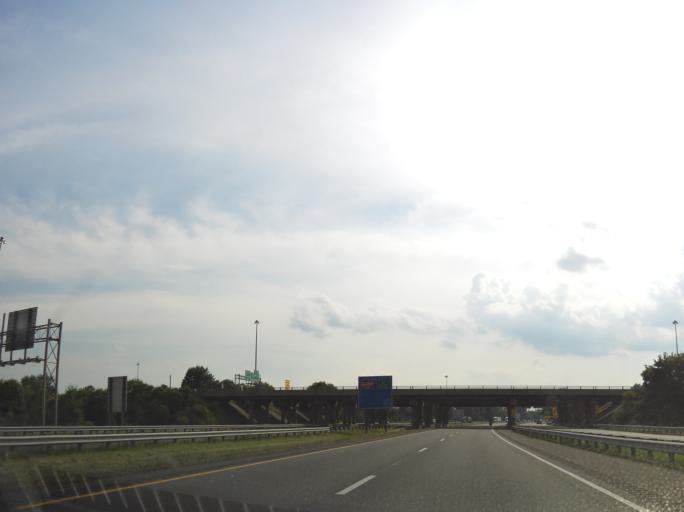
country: US
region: Maryland
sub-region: Washington County
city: Halfway
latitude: 39.6177
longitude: -77.7843
